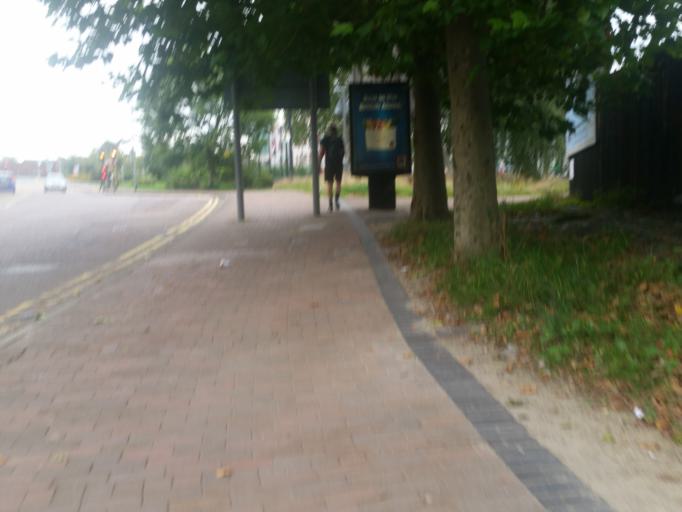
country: GB
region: England
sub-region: City and Borough of Salford
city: Salford
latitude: 53.4758
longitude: -2.2860
